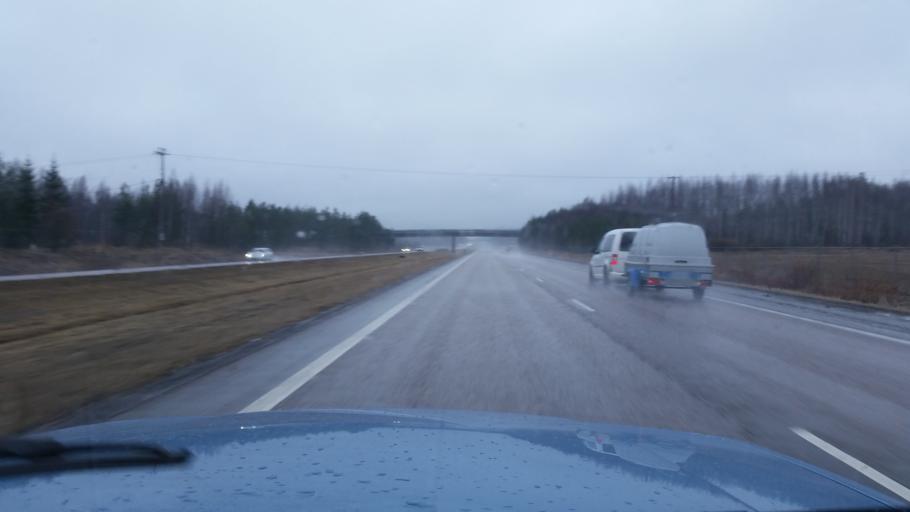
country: FI
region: Uusimaa
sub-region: Helsinki
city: Nurmijaervi
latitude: 60.5303
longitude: 24.8426
